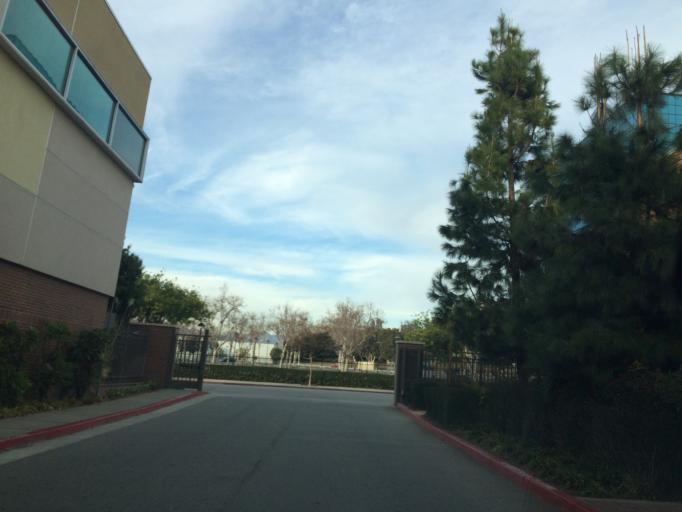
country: US
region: California
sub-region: Los Angeles County
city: Alhambra
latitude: 34.0837
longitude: -118.1509
